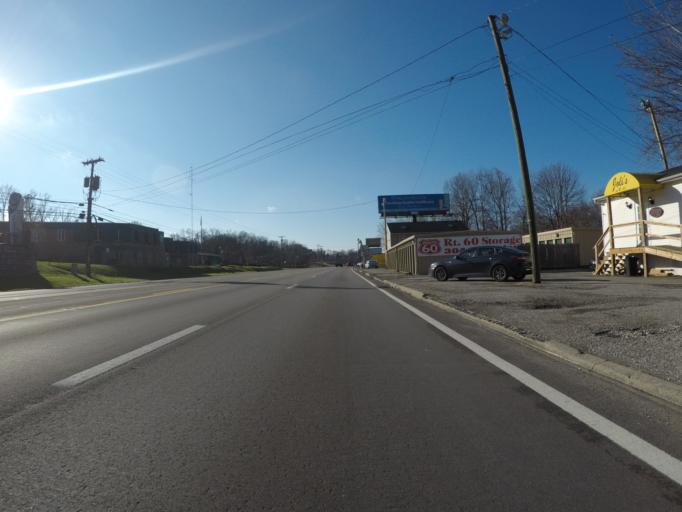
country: US
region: West Virginia
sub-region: Cabell County
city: Pea Ridge
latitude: 38.4111
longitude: -82.3729
